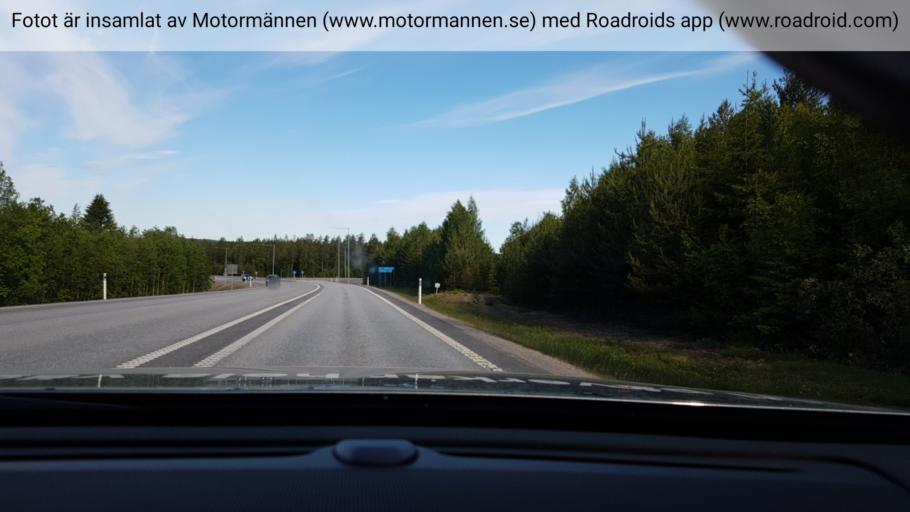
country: SE
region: Vaesterbotten
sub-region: Vannas Kommun
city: Vaennaes
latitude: 63.9217
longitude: 19.7859
